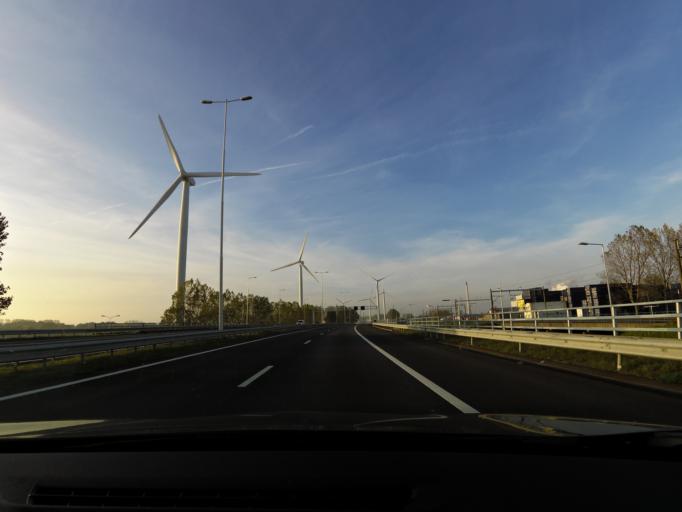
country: NL
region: South Holland
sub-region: Gemeente Brielle
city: Brielle
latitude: 51.9203
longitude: 4.1778
